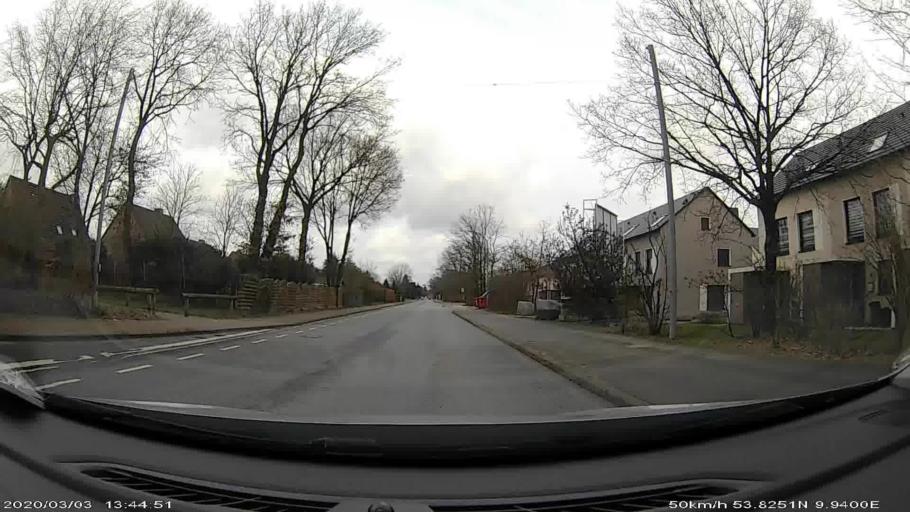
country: DE
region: Schleswig-Holstein
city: Kaltenkirchen
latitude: 53.8257
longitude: 9.9407
